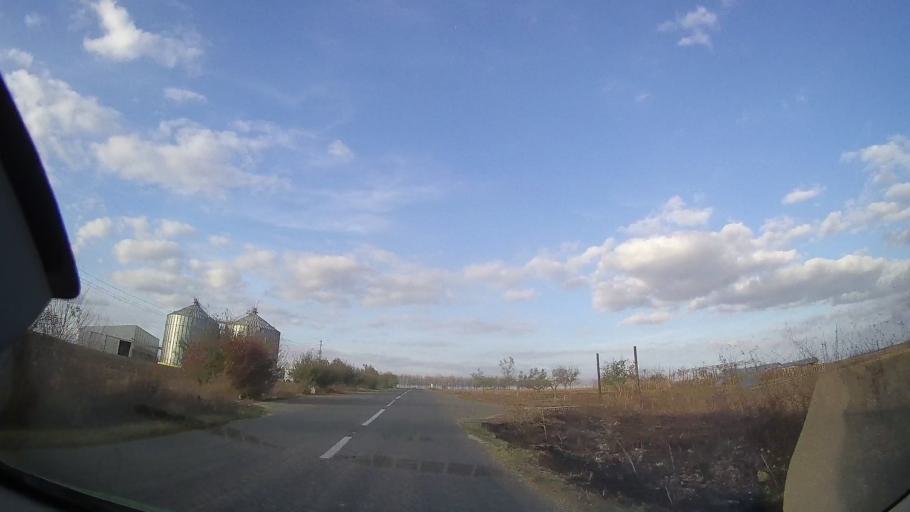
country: RO
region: Constanta
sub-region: Comuna Dumbraveni
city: Dumbraveni
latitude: 43.9256
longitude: 28.0297
